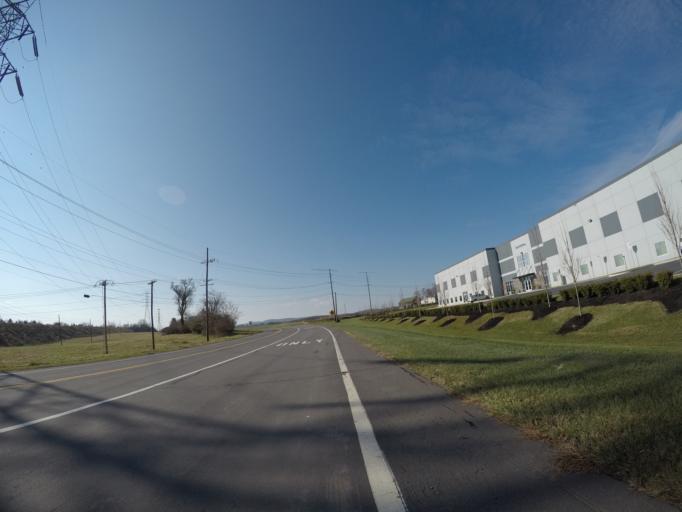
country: US
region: Maryland
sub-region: Frederick County
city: Ballenger Creek
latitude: 39.3614
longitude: -77.4422
